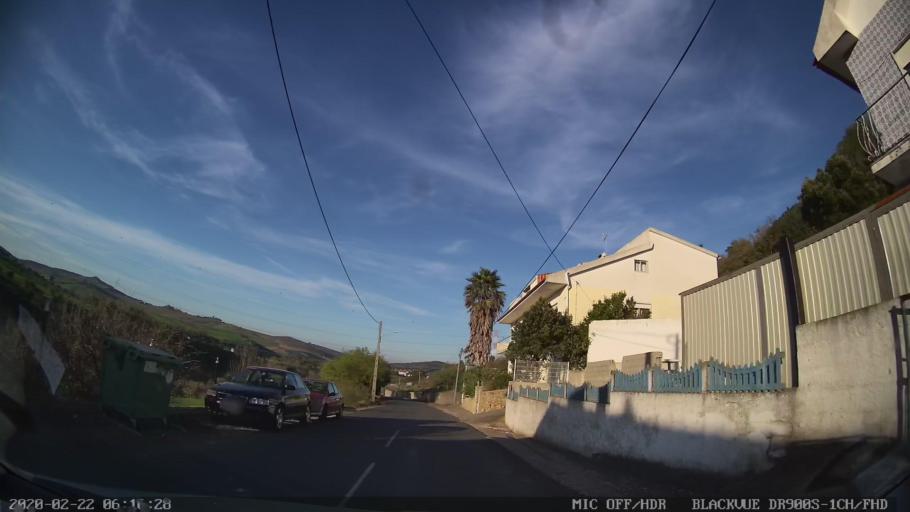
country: PT
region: Lisbon
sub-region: Vila Franca de Xira
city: Castanheira do Ribatejo
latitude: 38.9909
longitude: -9.0172
